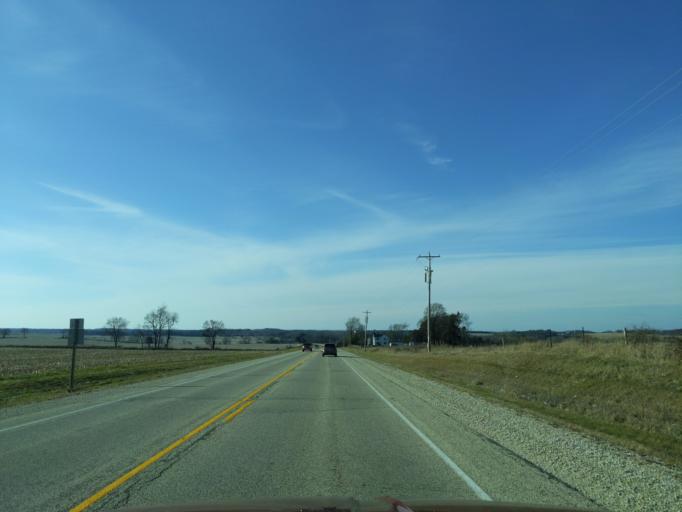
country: US
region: Wisconsin
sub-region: Jefferson County
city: Lake Koshkonong
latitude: 42.8297
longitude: -88.8588
